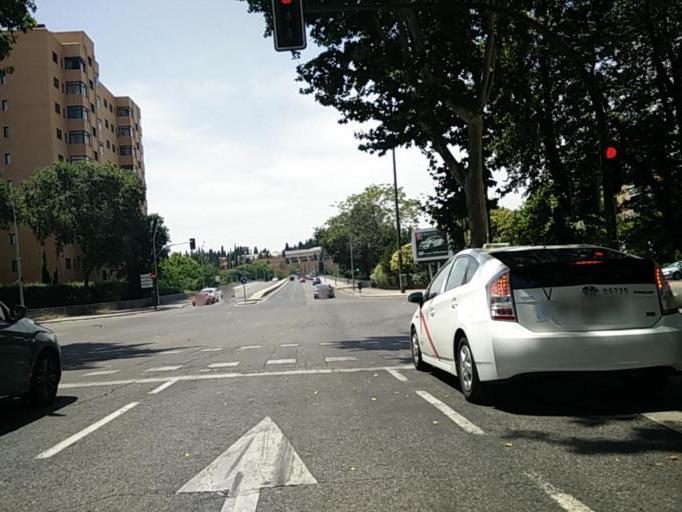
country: ES
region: Madrid
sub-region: Provincia de Madrid
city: Carabanchel
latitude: 40.4041
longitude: -3.7200
